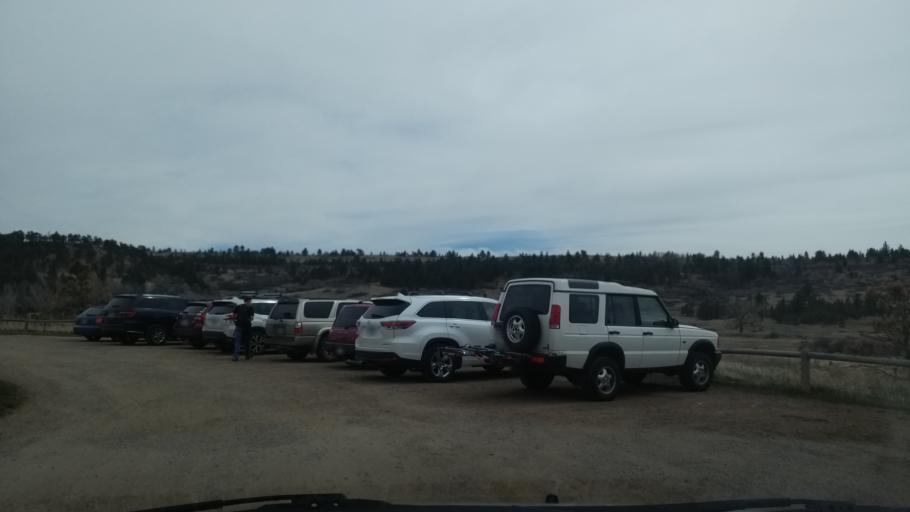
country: US
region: Colorado
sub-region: Boulder County
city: Superior
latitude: 39.9528
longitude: -105.2312
